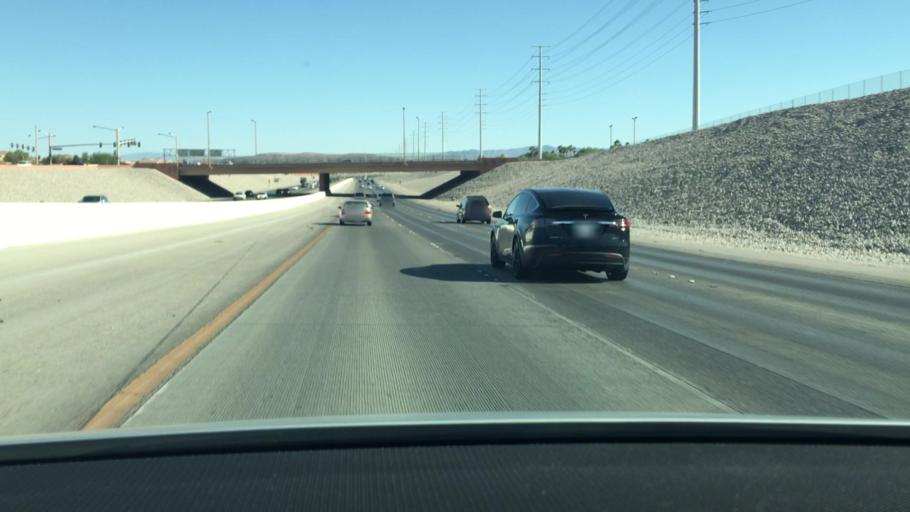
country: US
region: Nevada
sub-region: Clark County
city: Summerlin South
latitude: 36.1467
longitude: -115.3369
